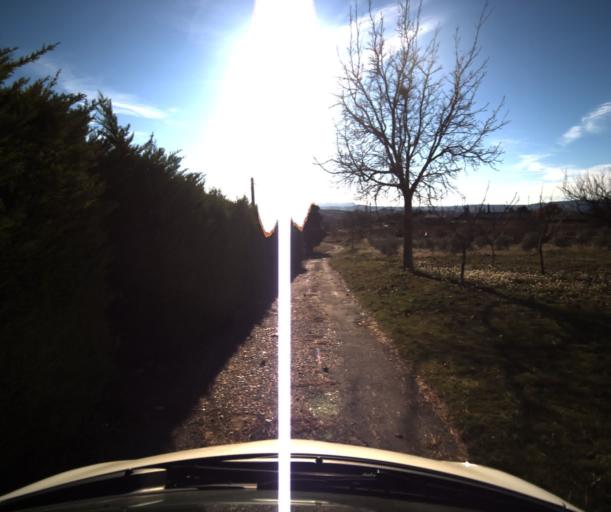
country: FR
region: Provence-Alpes-Cote d'Azur
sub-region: Departement du Vaucluse
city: Pertuis
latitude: 43.7190
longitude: 5.5147
